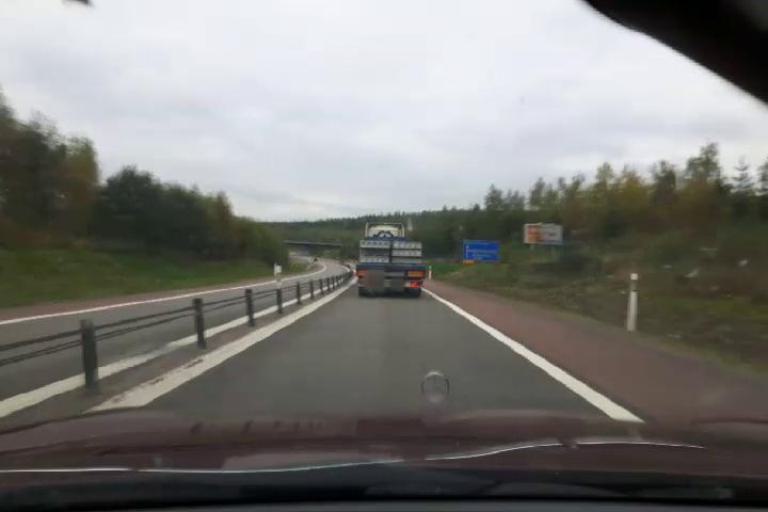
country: SE
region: Vaesternorrland
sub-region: Haernoesands Kommun
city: Haernoesand
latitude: 62.7848
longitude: 17.9191
